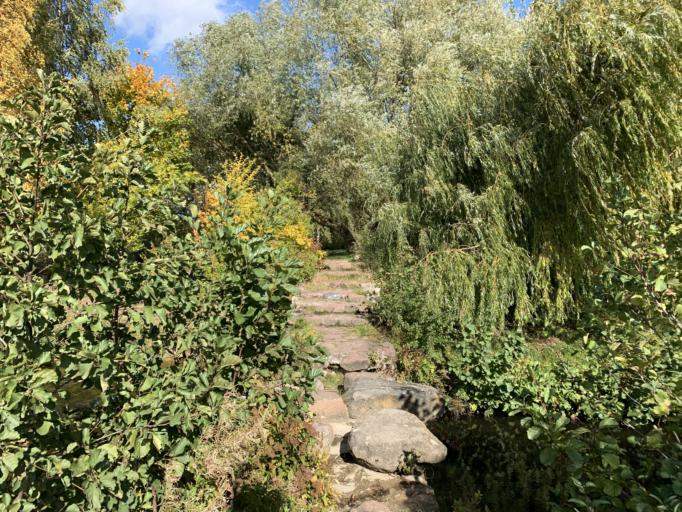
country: BY
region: Minsk
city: Nyasvizh
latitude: 53.2270
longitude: 26.7029
